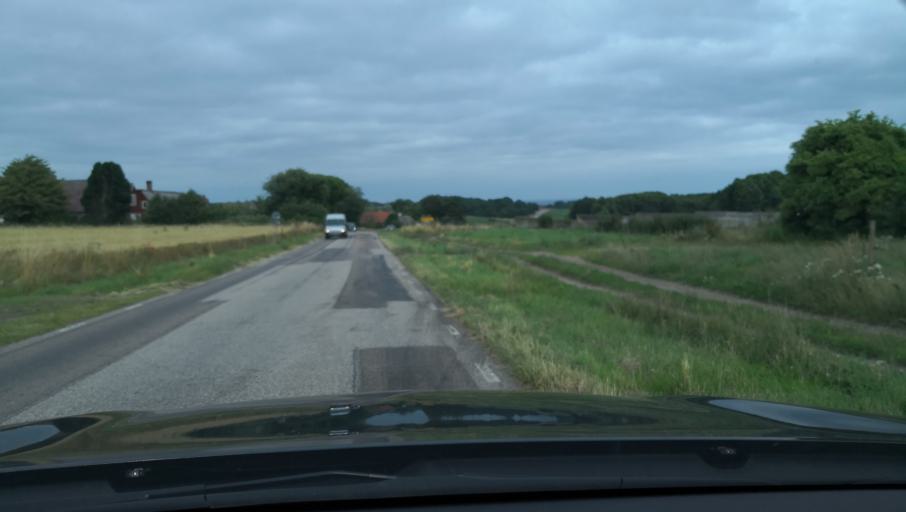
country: SE
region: Skane
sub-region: Simrishamns Kommun
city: Kivik
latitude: 55.6958
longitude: 14.1724
